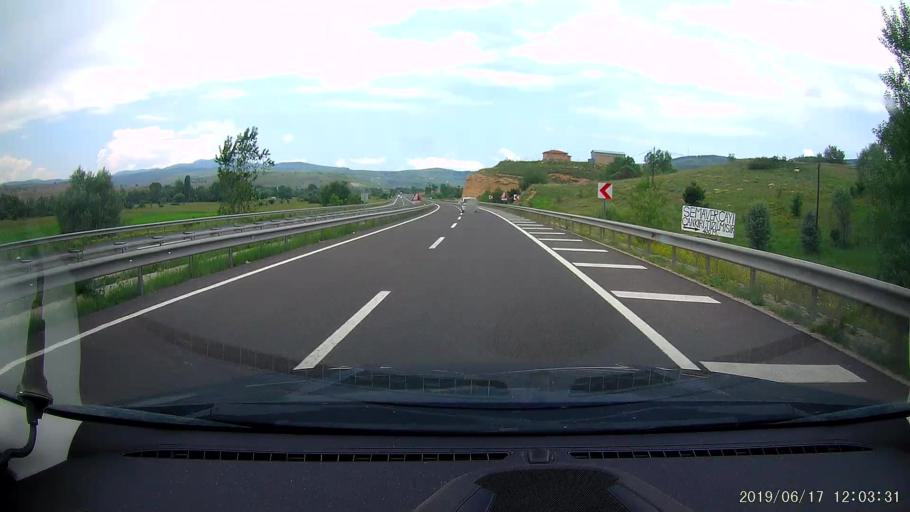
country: TR
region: Cankiri
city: Cerkes
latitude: 40.8258
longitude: 32.8213
